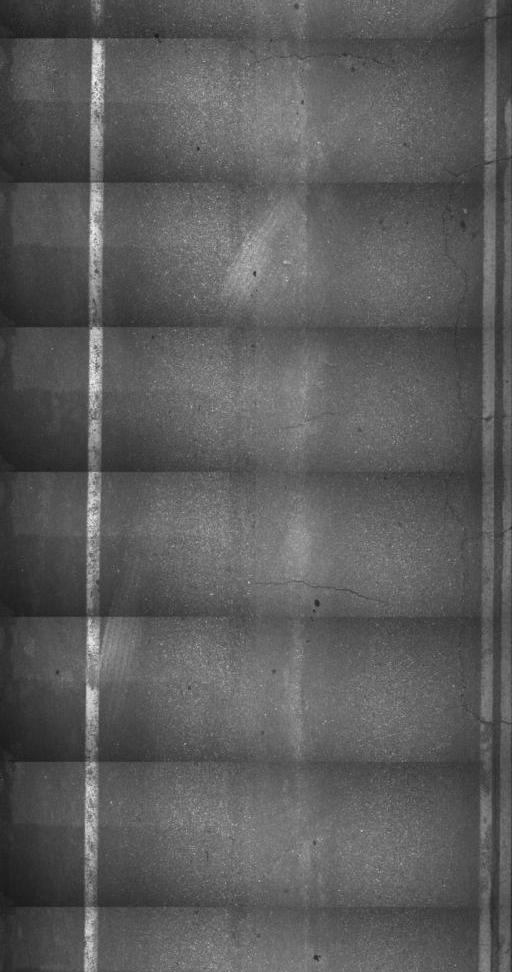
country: US
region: Vermont
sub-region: Orleans County
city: Newport
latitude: 44.8514
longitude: -72.4342
